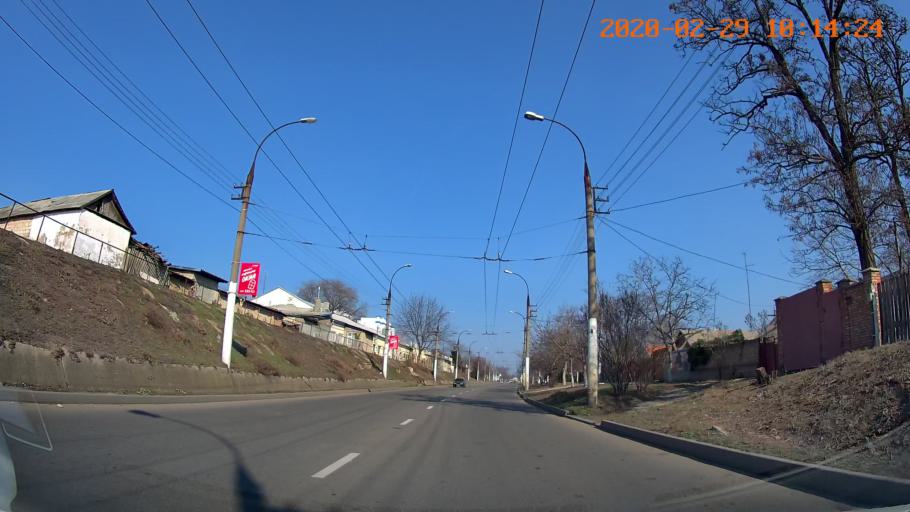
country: MD
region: Telenesti
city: Tiraspolul Nou
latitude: 46.8463
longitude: 29.6436
